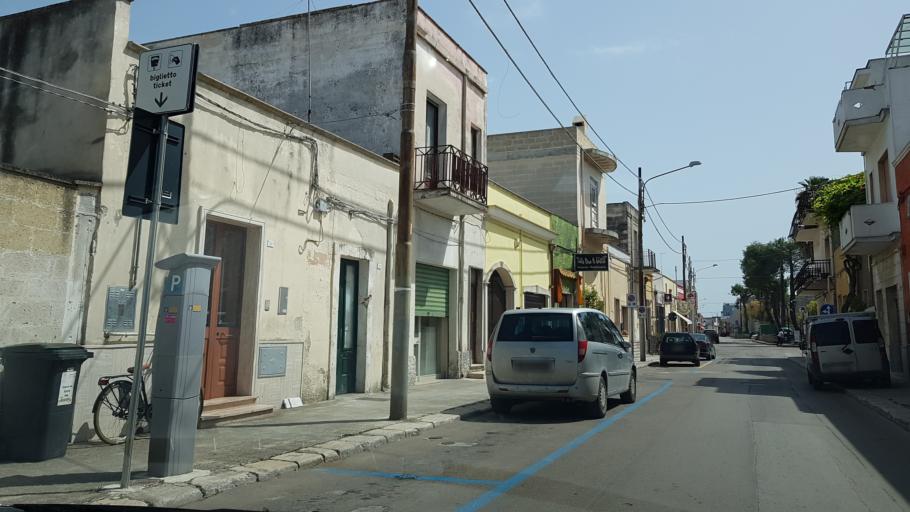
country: IT
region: Apulia
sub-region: Provincia di Brindisi
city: San Pancrazio Salentino
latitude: 40.4172
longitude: 17.8403
